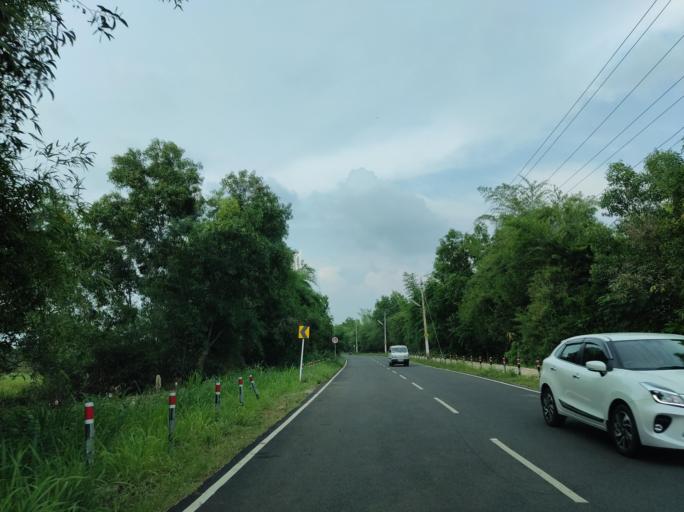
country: IN
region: Kerala
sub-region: Kottayam
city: Kottayam
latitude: 9.5704
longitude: 76.5224
